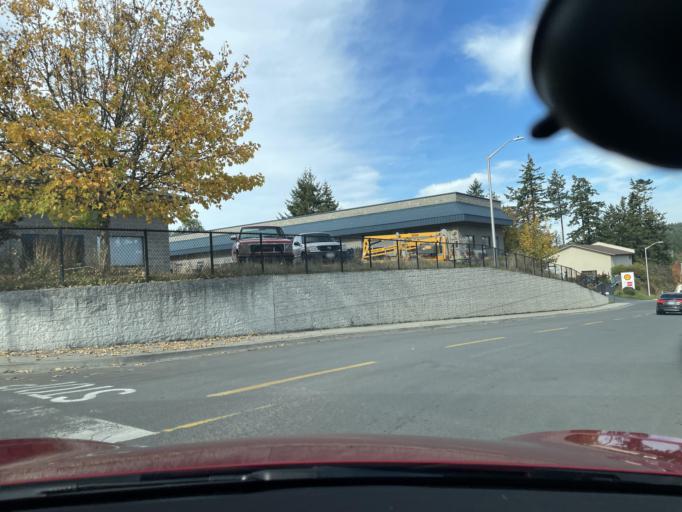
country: US
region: Washington
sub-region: San Juan County
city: Friday Harbor
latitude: 48.5363
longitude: -123.0285
